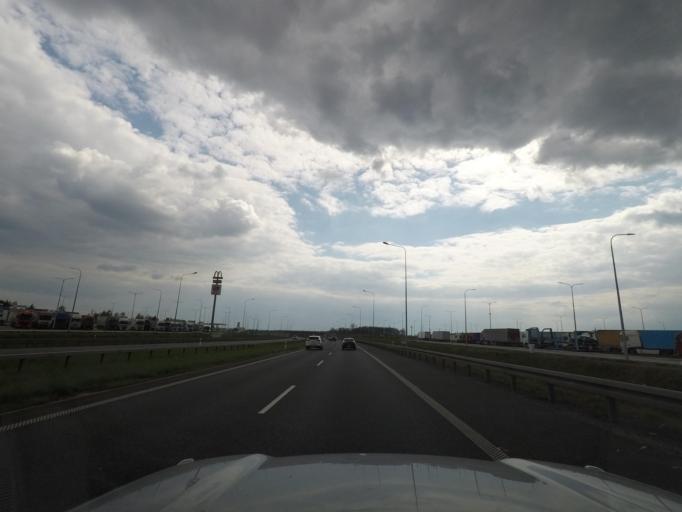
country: PL
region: Lower Silesian Voivodeship
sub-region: Legnica
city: Legnica
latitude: 51.2846
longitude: 16.1506
